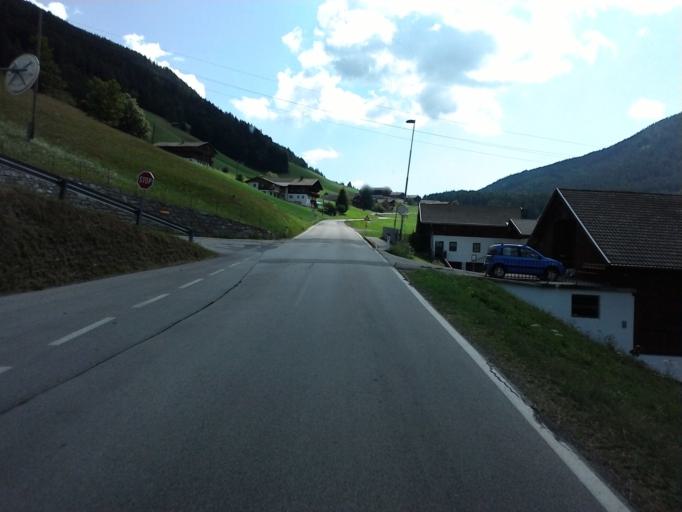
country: AT
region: Tyrol
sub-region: Politischer Bezirk Lienz
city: Kartitsch
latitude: 46.7220
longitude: 12.5137
